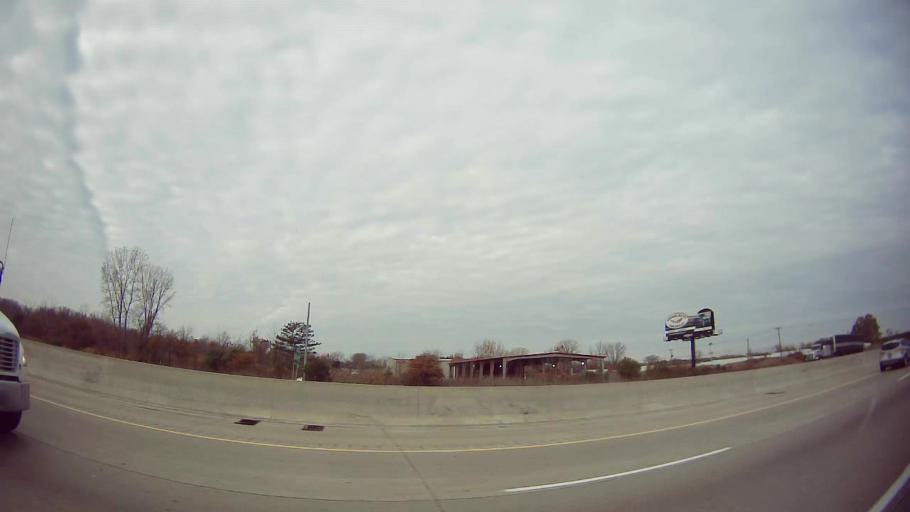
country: US
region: Michigan
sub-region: Wayne County
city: Woodhaven
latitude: 42.1680
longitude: -83.2431
